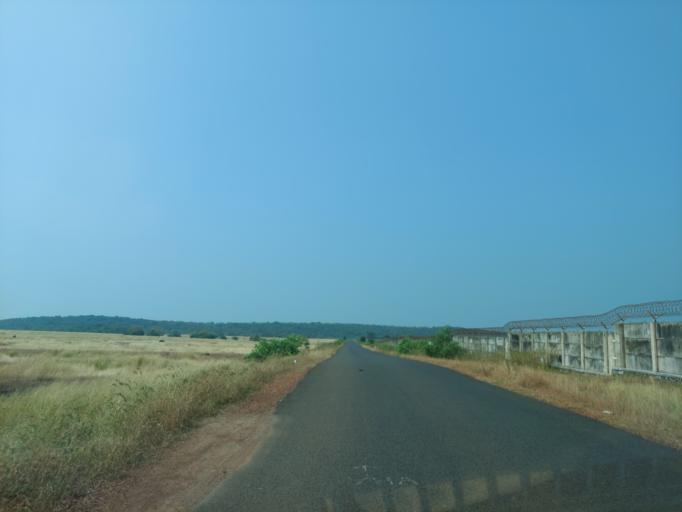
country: IN
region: Maharashtra
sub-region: Sindhudurg
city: Malvan
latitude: 15.9986
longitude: 73.5127
